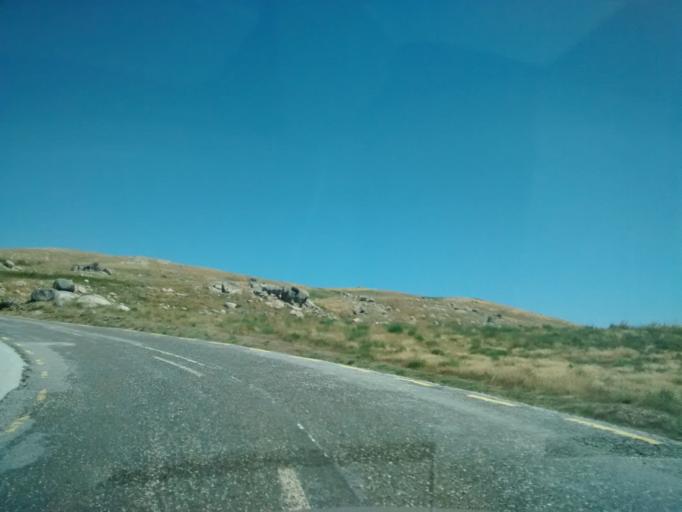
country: PT
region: Guarda
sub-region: Seia
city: Seia
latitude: 40.4137
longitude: -7.6399
